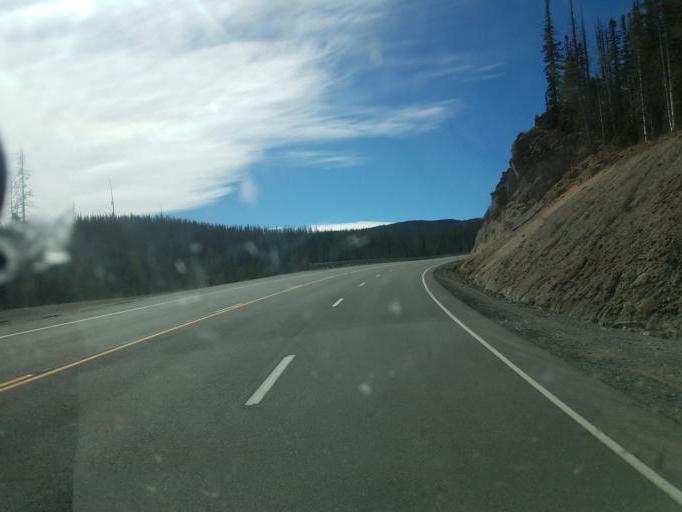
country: US
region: Colorado
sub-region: Archuleta County
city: Pagosa Springs
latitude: 37.4835
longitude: -106.7691
